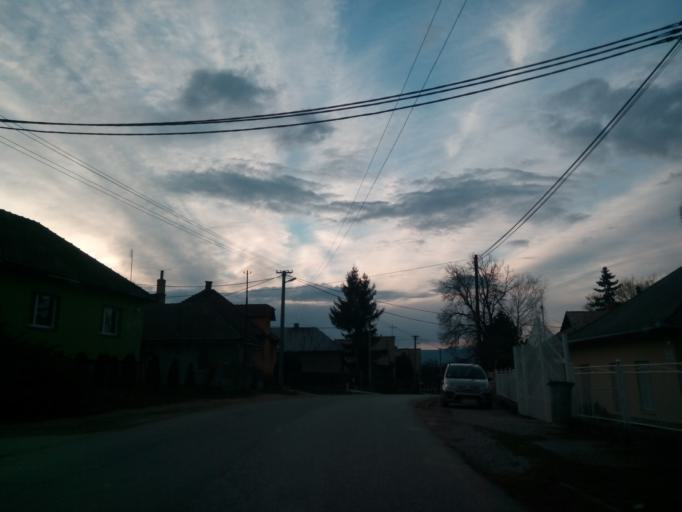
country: SK
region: Kosicky
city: Moldava nad Bodvou
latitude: 48.5576
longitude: 20.9629
